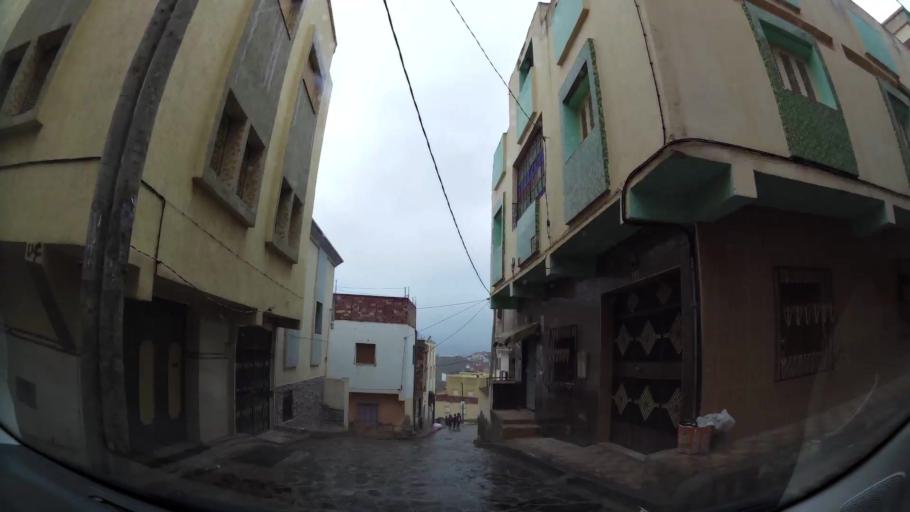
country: MA
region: Oriental
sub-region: Nador
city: Nador
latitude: 35.1831
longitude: -2.9361
